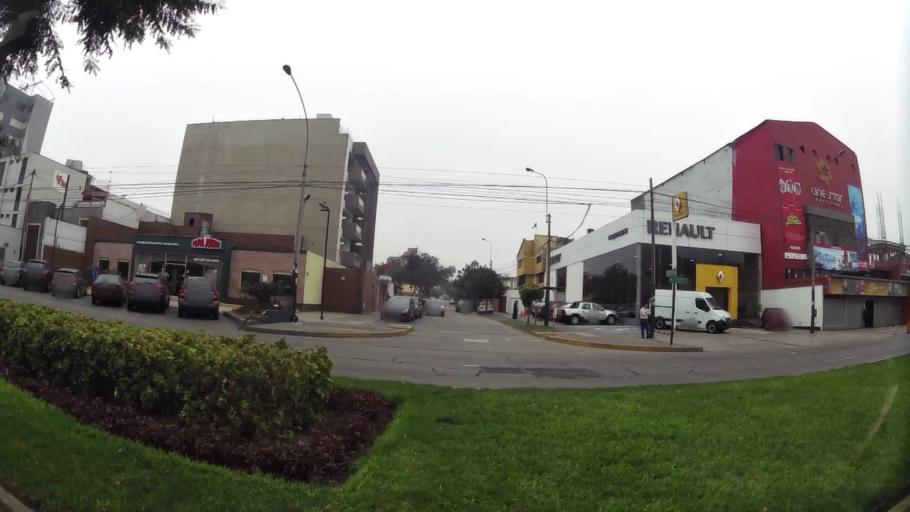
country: PE
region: Lima
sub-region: Lima
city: Surco
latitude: -12.1284
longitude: -76.9857
